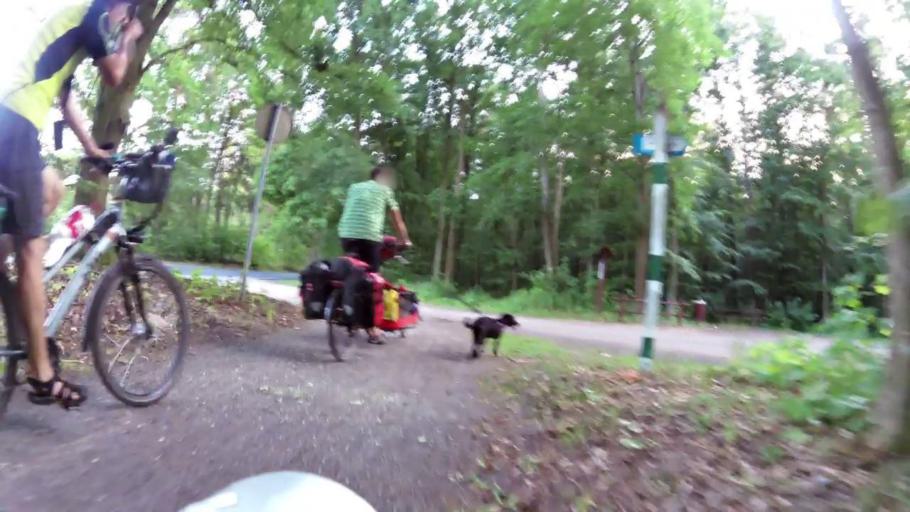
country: PL
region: Kujawsko-Pomorskie
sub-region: Powiat bydgoski
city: Dabrowa Chelminska
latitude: 53.1665
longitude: 18.2549
